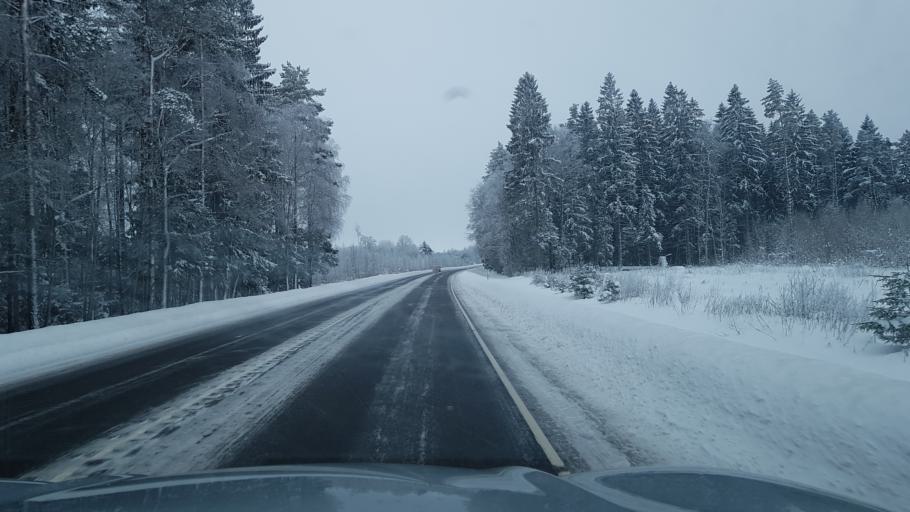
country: EE
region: Ida-Virumaa
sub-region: Johvi vald
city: Johvi
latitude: 59.2899
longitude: 27.3992
